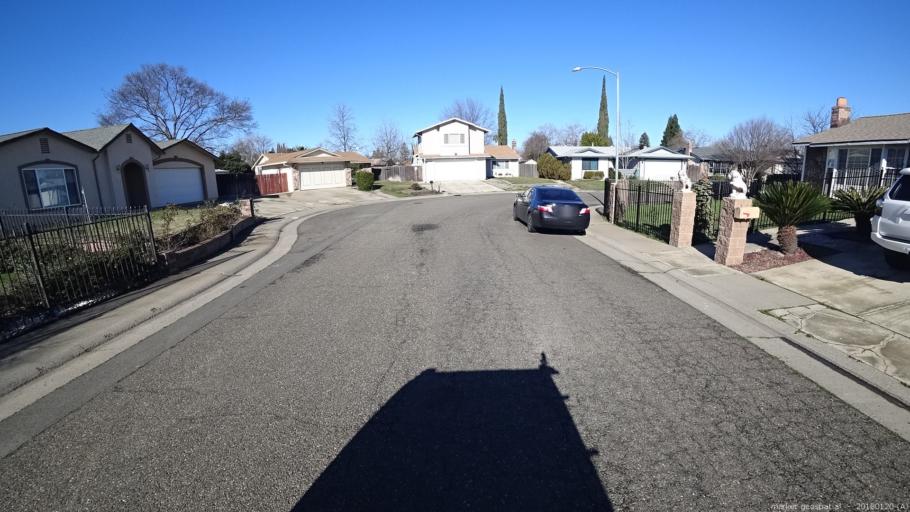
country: US
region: California
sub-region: Sacramento County
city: Rancho Cordova
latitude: 38.5725
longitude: -121.3115
